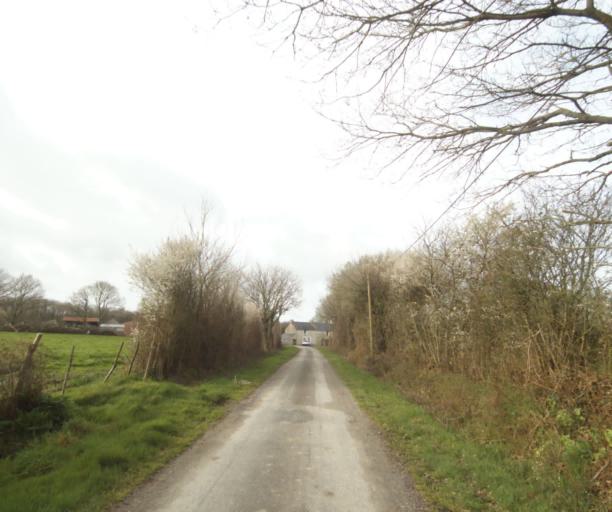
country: FR
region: Pays de la Loire
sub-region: Departement de la Loire-Atlantique
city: Bouvron
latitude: 47.4042
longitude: -1.8897
